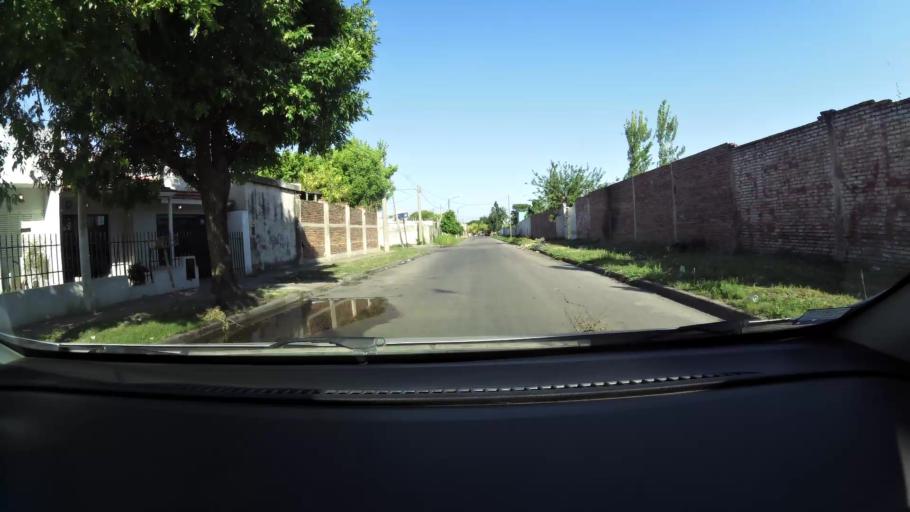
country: AR
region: Cordoba
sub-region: Departamento de Capital
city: Cordoba
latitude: -31.3851
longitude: -64.1670
